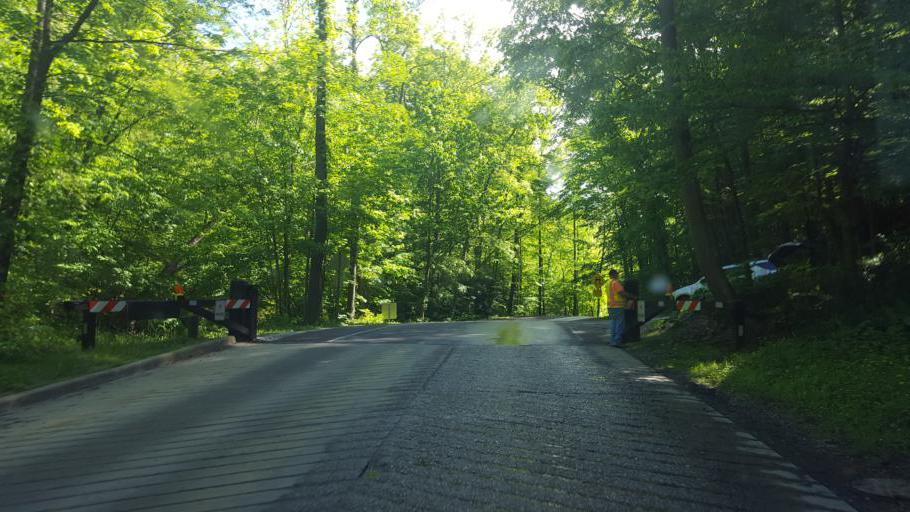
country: US
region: Ohio
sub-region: Summit County
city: Fairlawn
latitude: 41.1357
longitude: -81.5696
